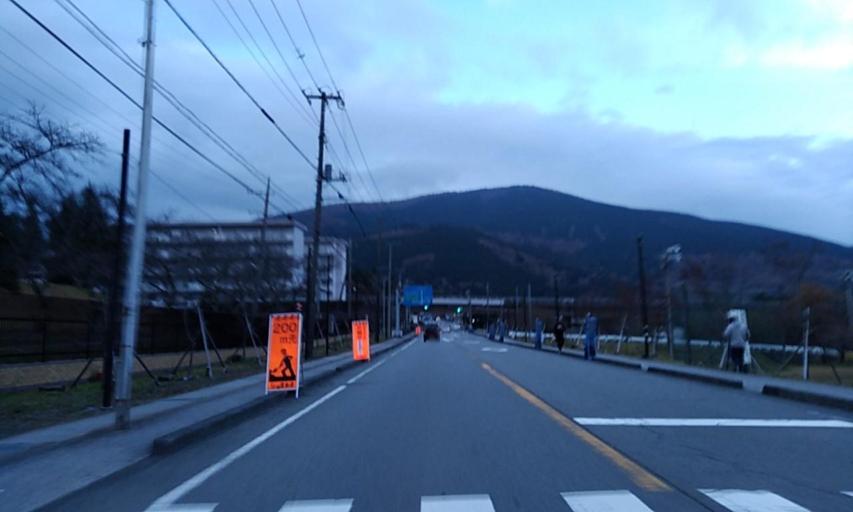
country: JP
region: Shizuoka
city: Gotemba
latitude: 35.3589
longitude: 138.8639
